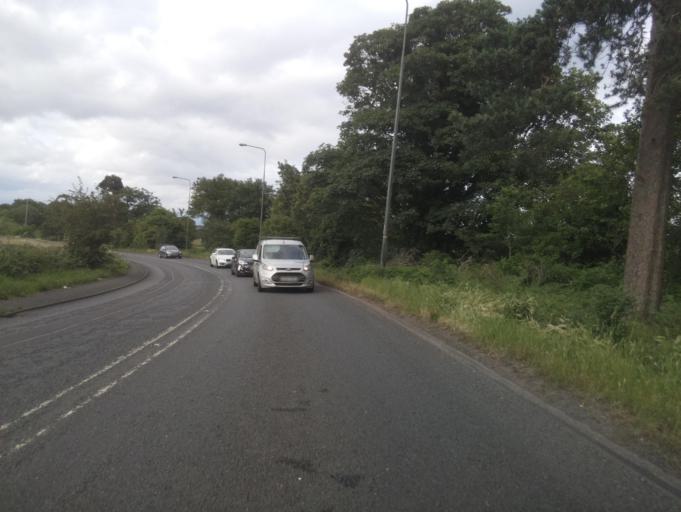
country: GB
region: England
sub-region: Worcestershire
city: Kidderminster
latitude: 52.4164
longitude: -2.2204
